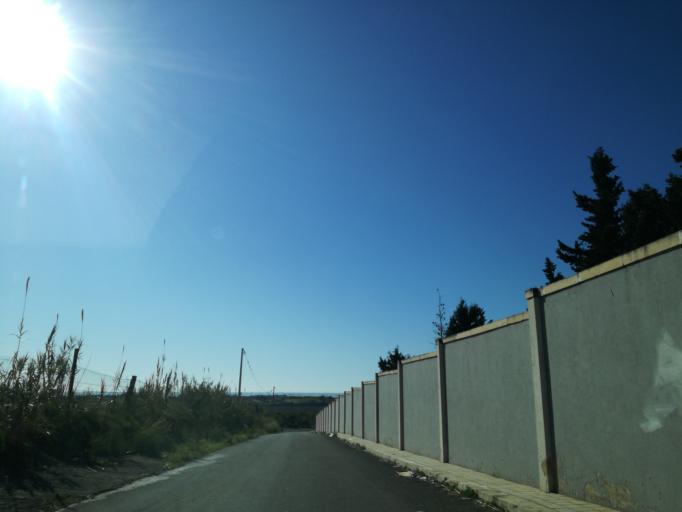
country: IT
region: Sicily
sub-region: Provincia di Caltanissetta
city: Gela
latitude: 37.0575
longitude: 14.3201
